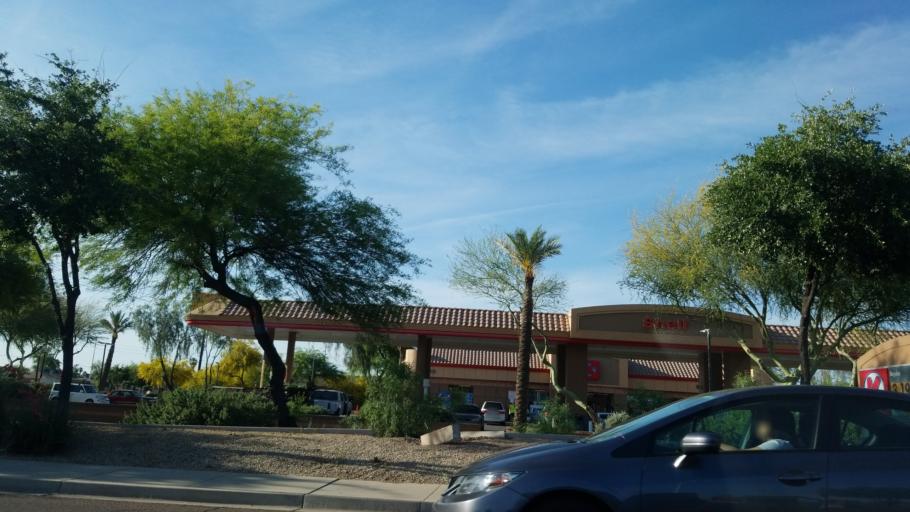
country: US
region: Arizona
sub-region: Maricopa County
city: Chandler
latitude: 33.3063
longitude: -111.8235
